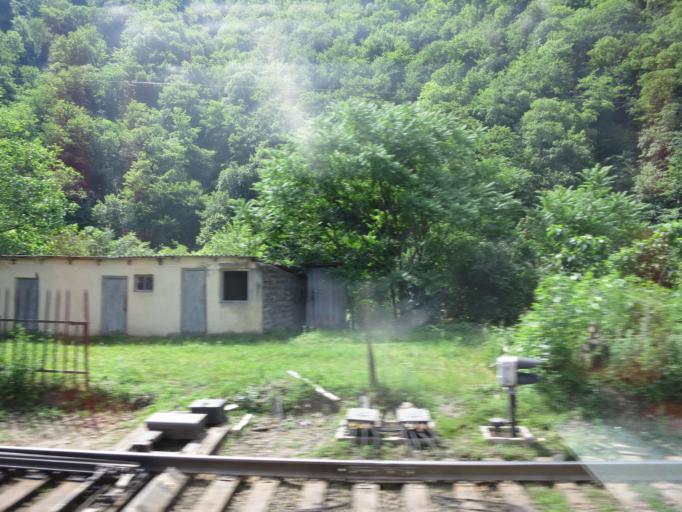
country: GE
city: Surami
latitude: 41.9978
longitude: 43.4362
